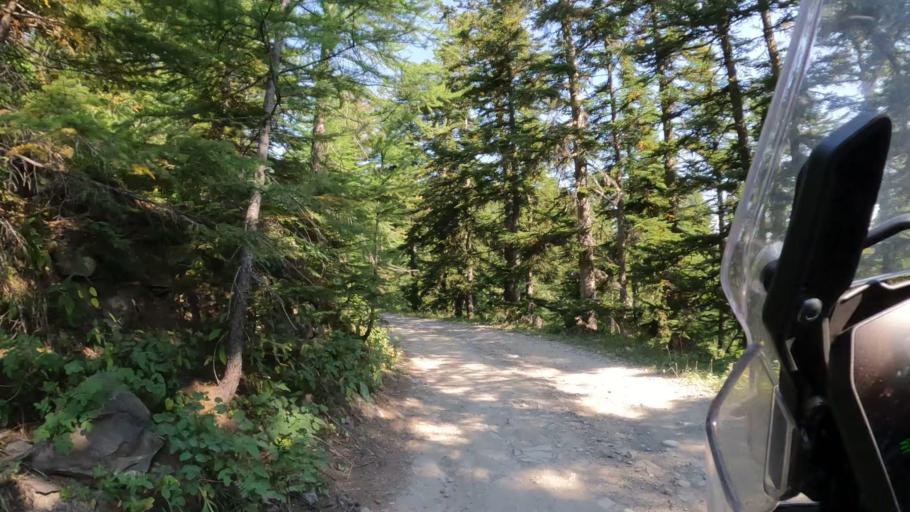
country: FR
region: Provence-Alpes-Cote d'Azur
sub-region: Departement des Hautes-Alpes
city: Embrun
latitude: 44.5927
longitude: 6.5739
